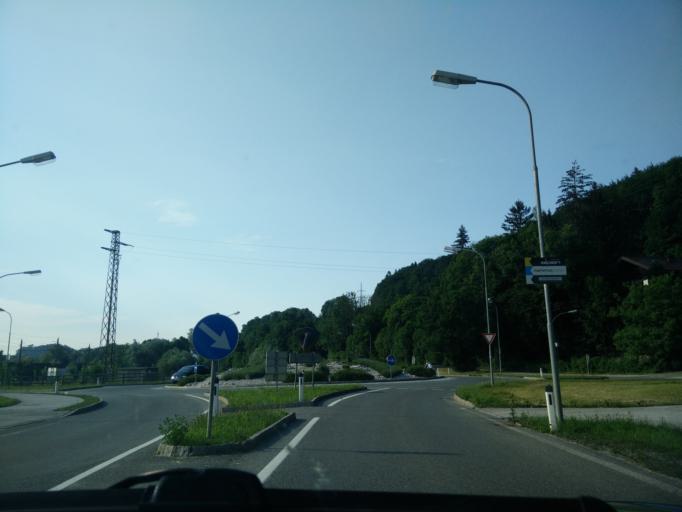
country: AT
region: Salzburg
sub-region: Politischer Bezirk Salzburg-Umgebung
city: Elsbethen
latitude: 47.7364
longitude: 13.0891
